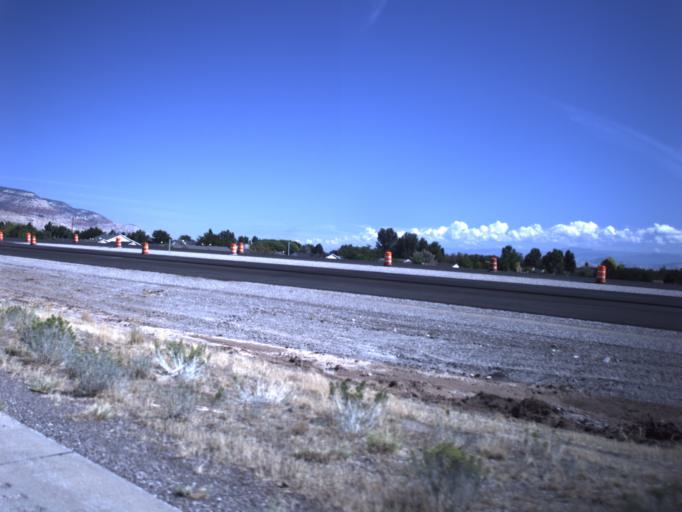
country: US
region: Utah
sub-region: Sevier County
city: Richfield
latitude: 38.7534
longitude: -112.1053
